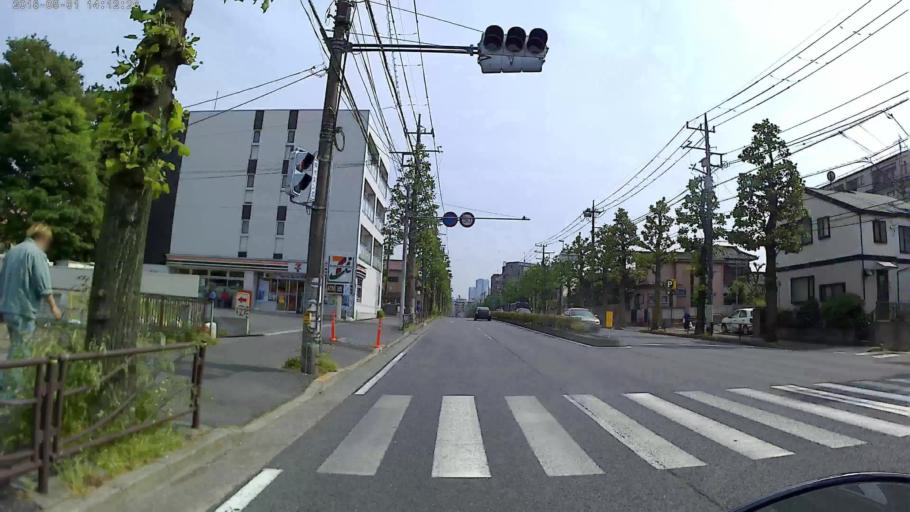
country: JP
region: Kanagawa
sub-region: Kawasaki-shi
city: Kawasaki
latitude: 35.5710
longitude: 139.6695
